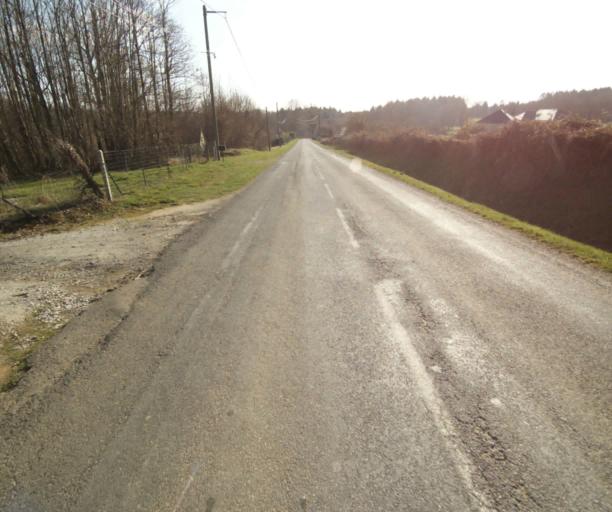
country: FR
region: Limousin
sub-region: Departement de la Correze
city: Saint-Clement
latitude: 45.3496
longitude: 1.6279
